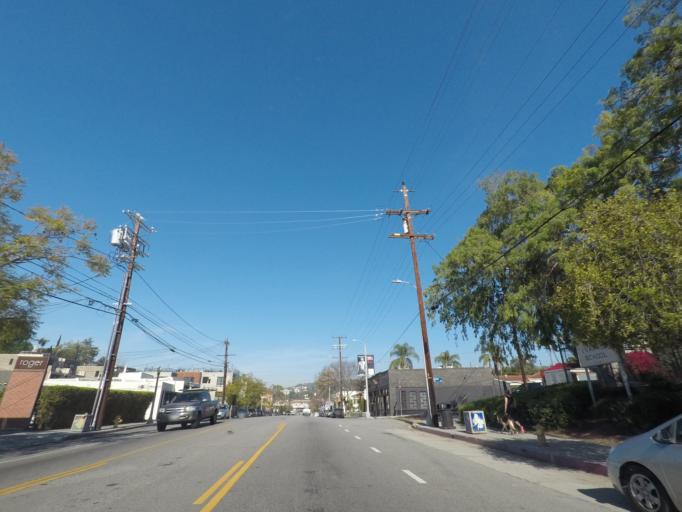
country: US
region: California
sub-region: Los Angeles County
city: Silver Lake
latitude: 34.1082
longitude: -118.2677
